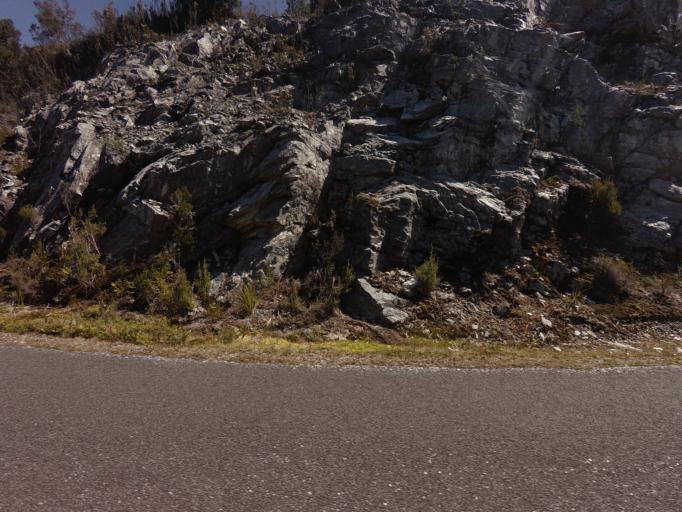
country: AU
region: Tasmania
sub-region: West Coast
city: Queenstown
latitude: -42.7451
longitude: 145.9806
